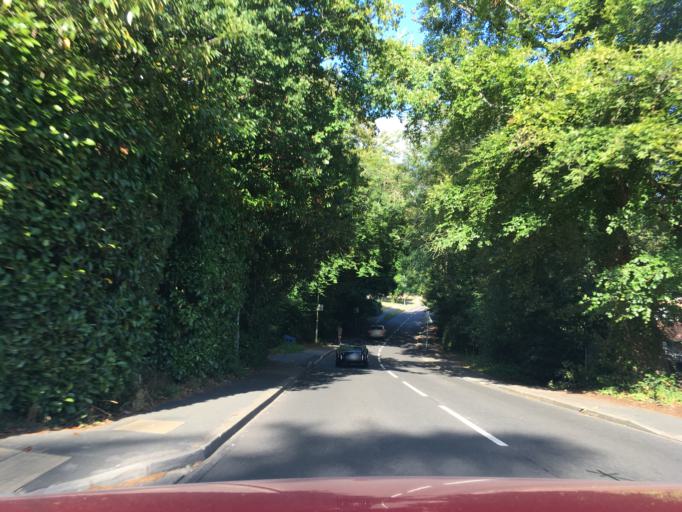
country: GB
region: England
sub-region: Hampshire
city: Chandlers Ford
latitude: 50.9993
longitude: -1.3913
